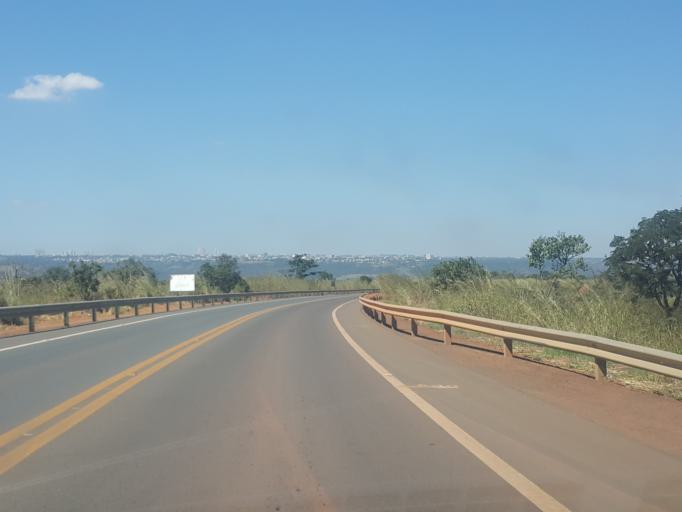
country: BR
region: Goias
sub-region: Luziania
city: Luziania
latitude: -16.0082
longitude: -48.1505
